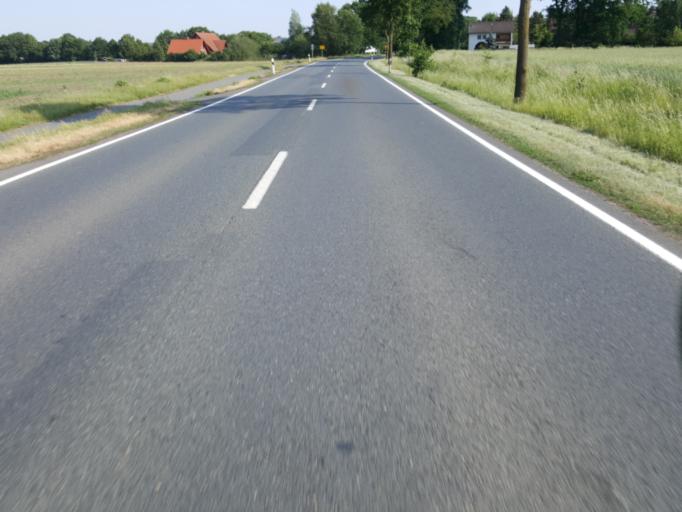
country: DE
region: Lower Saxony
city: Estorf
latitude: 52.5825
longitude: 9.1390
